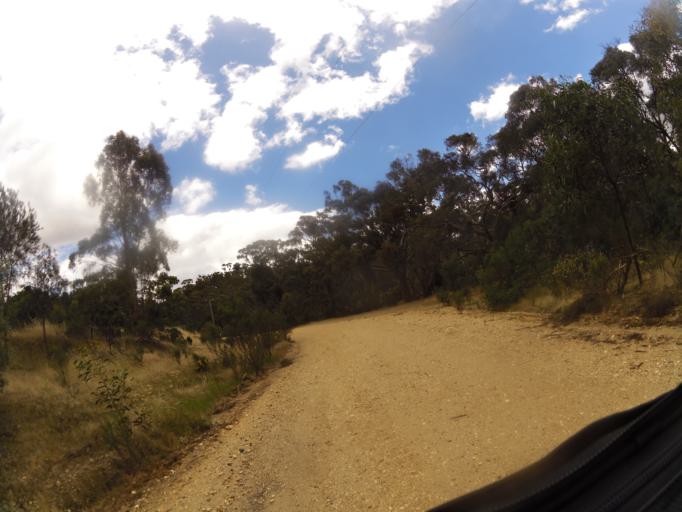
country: AU
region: Victoria
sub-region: Mount Alexander
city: Castlemaine
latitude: -37.0529
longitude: 144.2719
